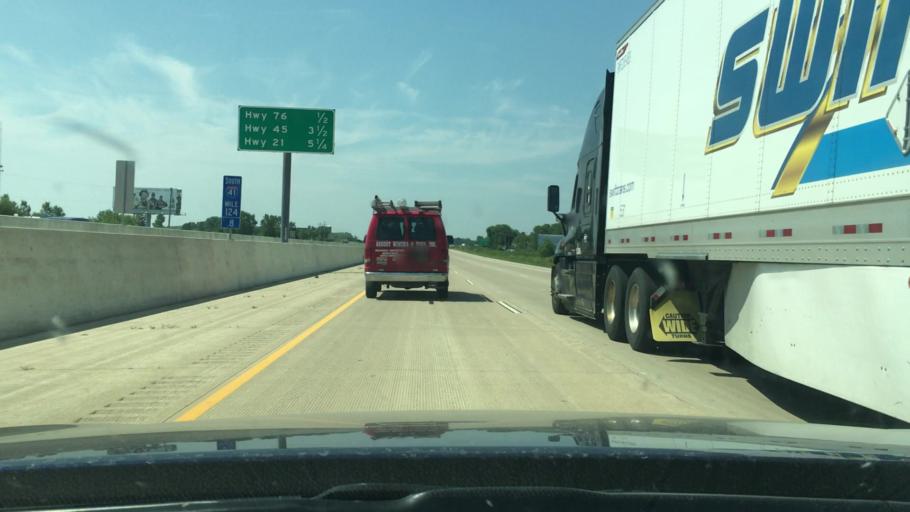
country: US
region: Wisconsin
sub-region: Winnebago County
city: Oshkosh
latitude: 44.1048
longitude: -88.5321
